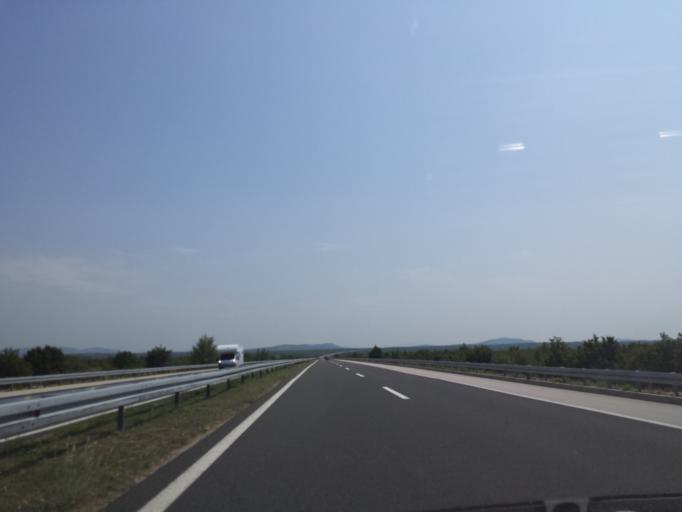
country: HR
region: Zadarska
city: Benkovac
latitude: 44.0017
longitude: 15.6019
